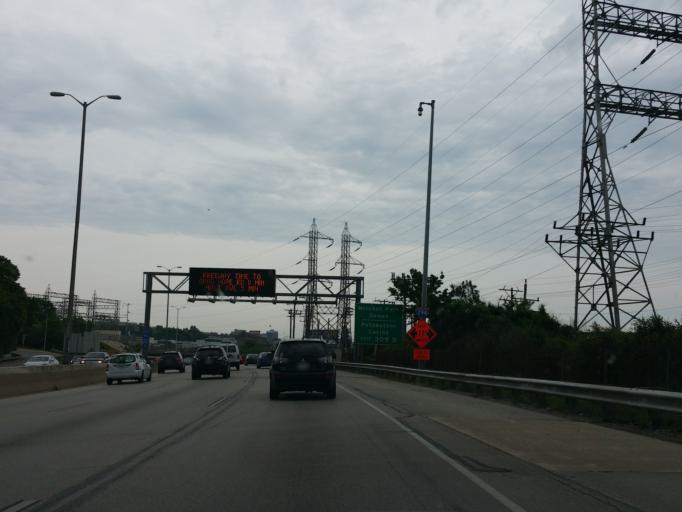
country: US
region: Wisconsin
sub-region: Milwaukee County
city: West Milwaukee
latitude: 43.0323
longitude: -87.9521
